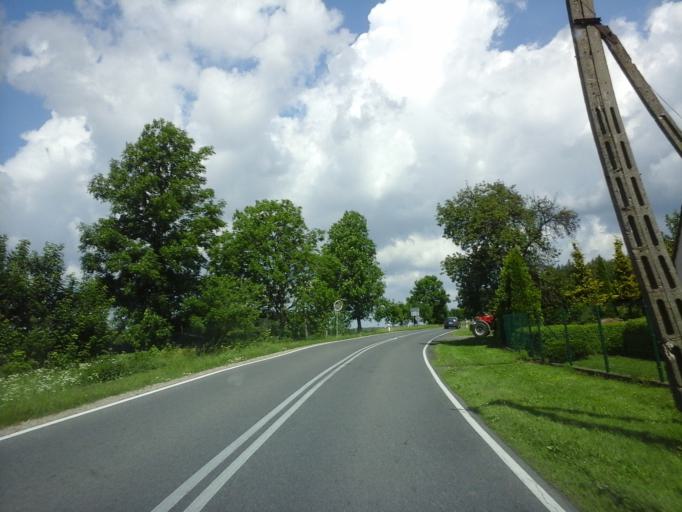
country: PL
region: West Pomeranian Voivodeship
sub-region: Powiat swidwinski
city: Slawoborze
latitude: 53.8401
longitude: 15.7396
